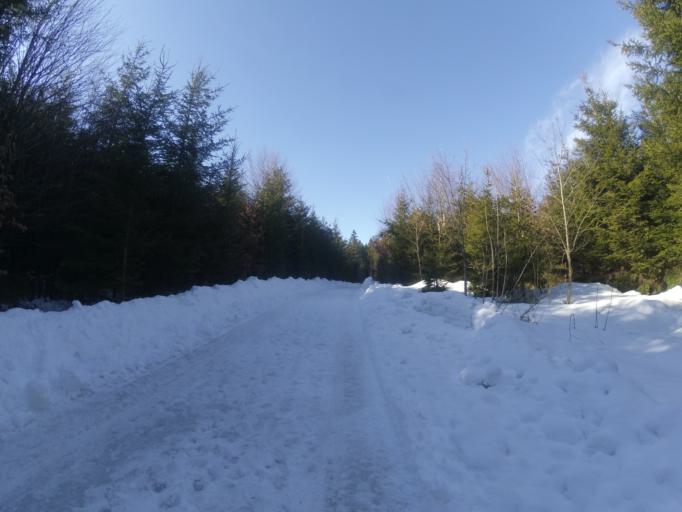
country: DE
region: Bavaria
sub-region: Upper Bavaria
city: Aying
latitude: 47.9872
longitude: 11.7510
